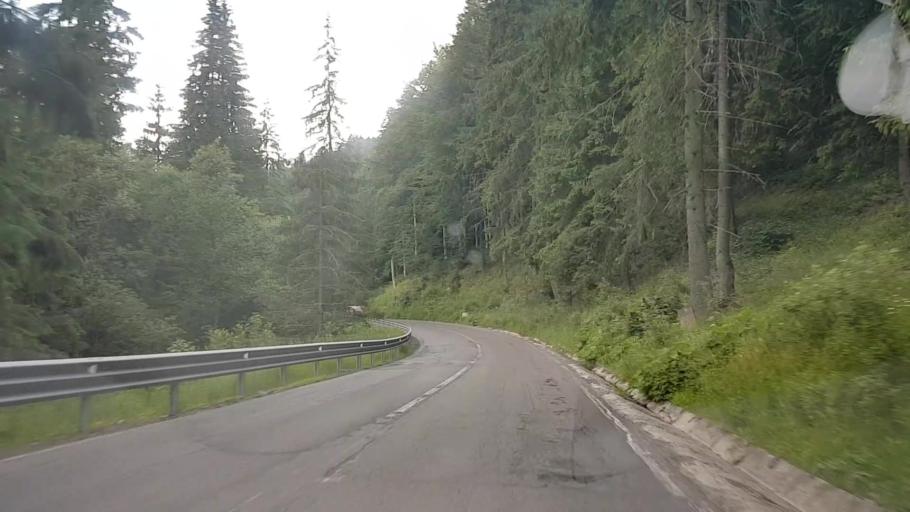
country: RO
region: Harghita
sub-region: Comuna Varsag
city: Varsag
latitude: 46.6273
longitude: 25.2579
